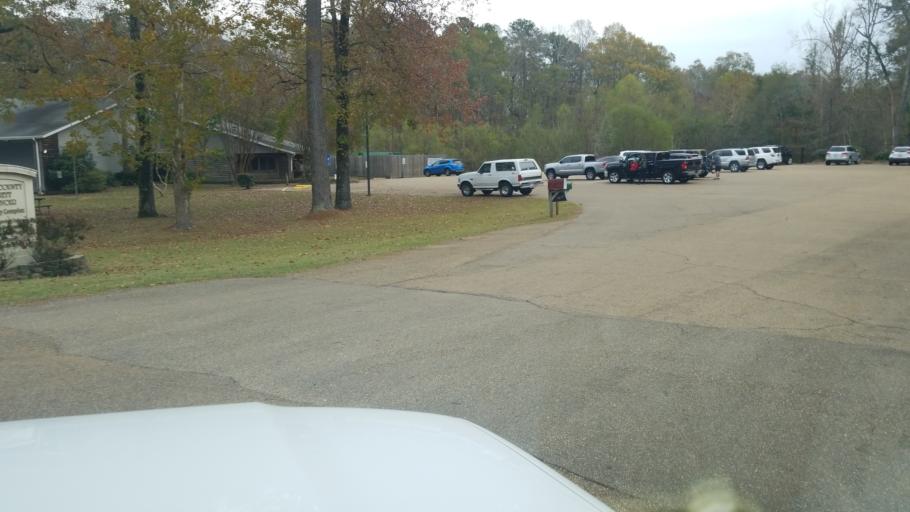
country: US
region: Mississippi
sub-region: Rankin County
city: Brandon
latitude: 32.3719
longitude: -90.0132
